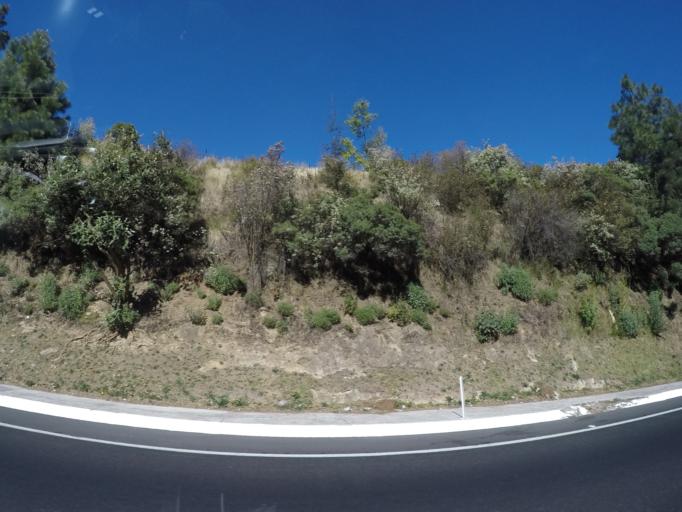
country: MX
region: Mexico City
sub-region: Cuajimalpa de Morelos
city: San Lorenzo Acopilco
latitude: 19.3180
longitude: -99.3280
